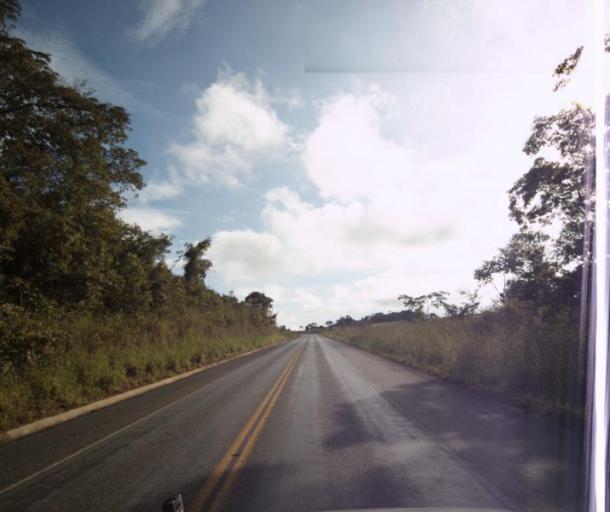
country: BR
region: Goias
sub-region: Padre Bernardo
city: Padre Bernardo
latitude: -15.4845
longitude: -48.6176
